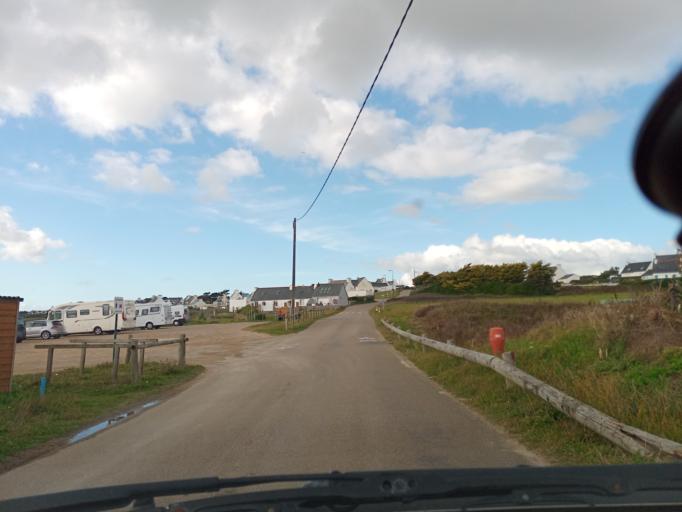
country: FR
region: Brittany
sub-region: Departement du Finistere
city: Plozevet
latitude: 47.9798
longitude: -4.4490
